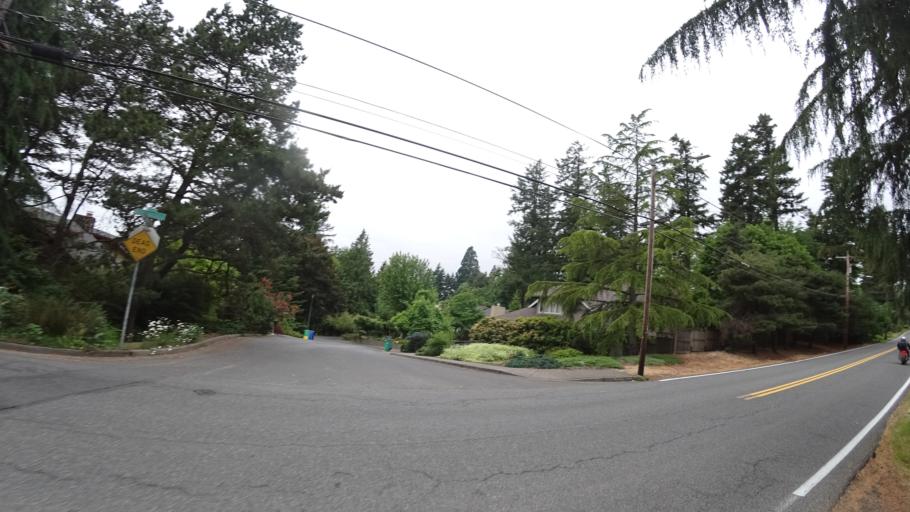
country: US
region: Oregon
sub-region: Multnomah County
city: Portland
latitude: 45.4872
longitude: -122.7103
